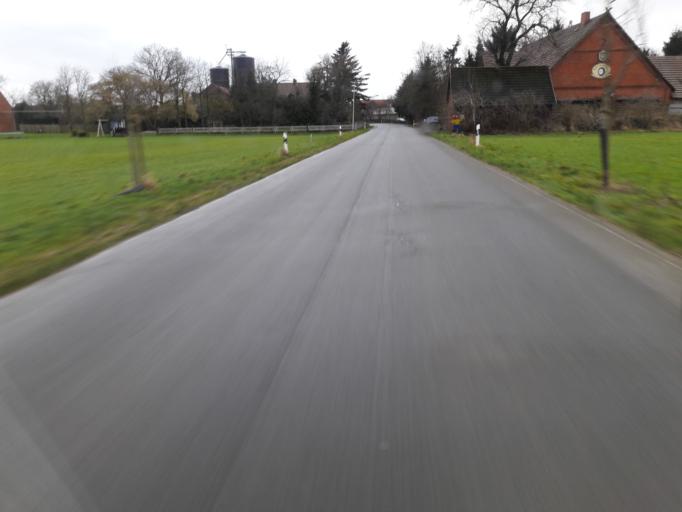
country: DE
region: Lower Saxony
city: Raddestorf
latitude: 52.4486
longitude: 8.9906
